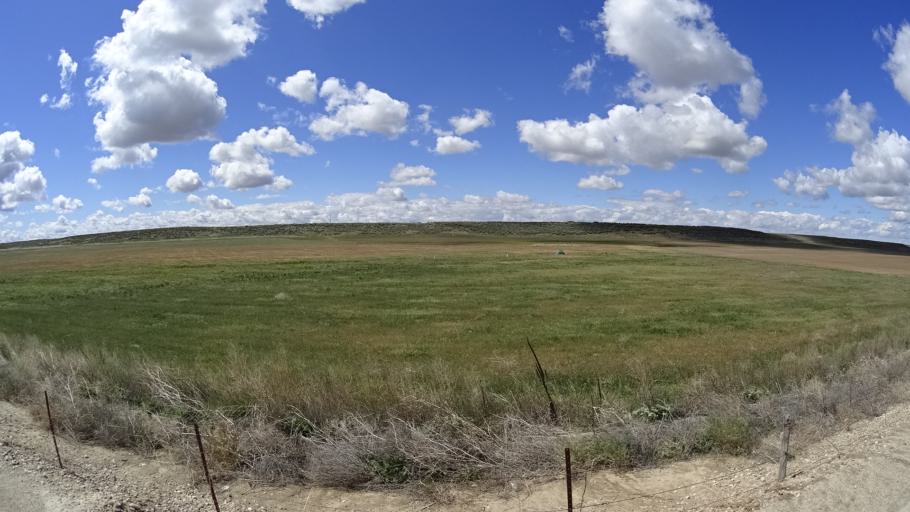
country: US
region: Idaho
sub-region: Ada County
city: Boise
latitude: 43.4852
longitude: -116.2517
